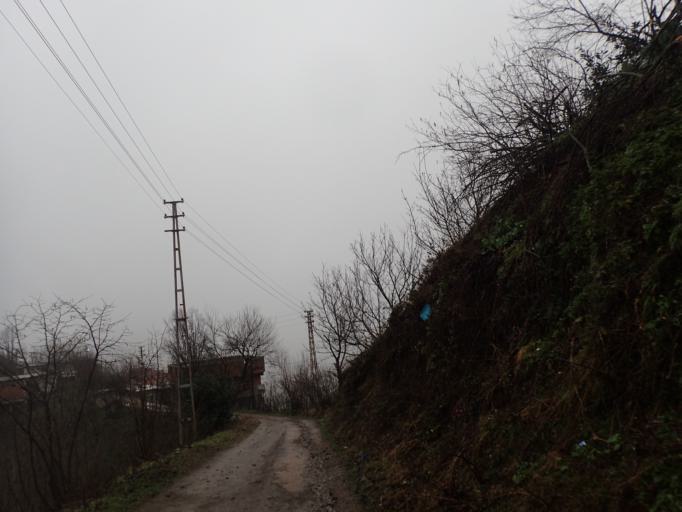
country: TR
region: Ordu
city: Camas
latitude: 40.9124
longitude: 37.5682
